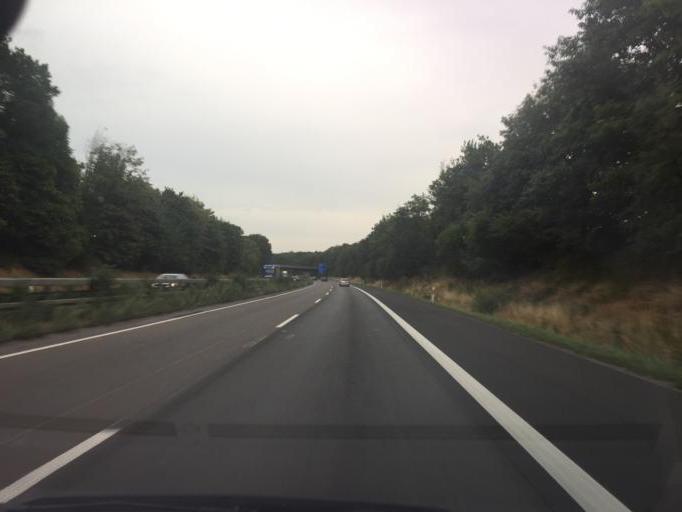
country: DE
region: North Rhine-Westphalia
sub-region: Regierungsbezirk Dusseldorf
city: Viersen
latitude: 51.2253
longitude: 6.3649
